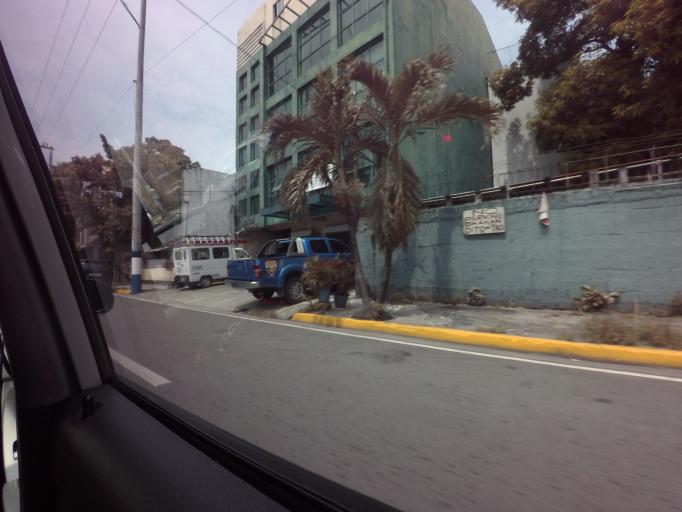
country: PH
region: Metro Manila
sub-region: City of Manila
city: Quiapo
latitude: 14.5754
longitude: 120.9931
